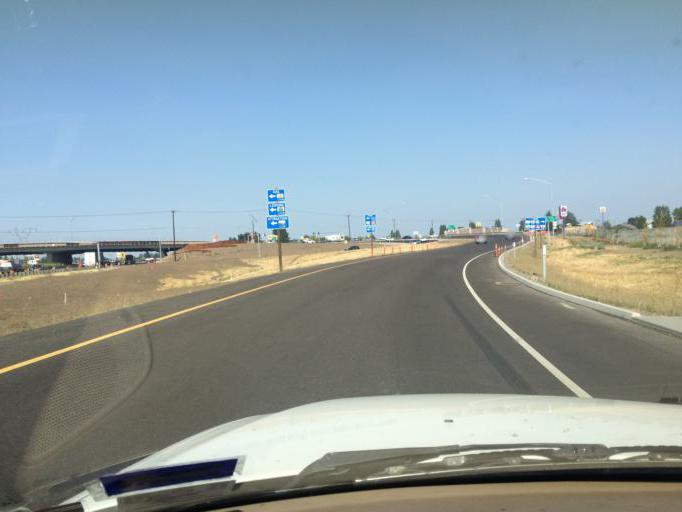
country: US
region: Oregon
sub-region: Marion County
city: Woodburn
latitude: 45.1492
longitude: -122.8820
